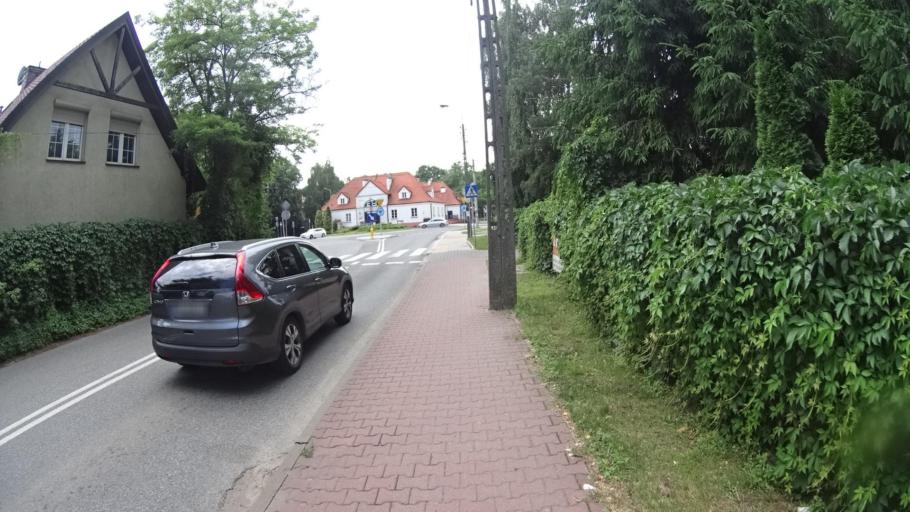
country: PL
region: Masovian Voivodeship
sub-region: Powiat pruszkowski
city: Nadarzyn
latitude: 52.0948
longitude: 20.8075
